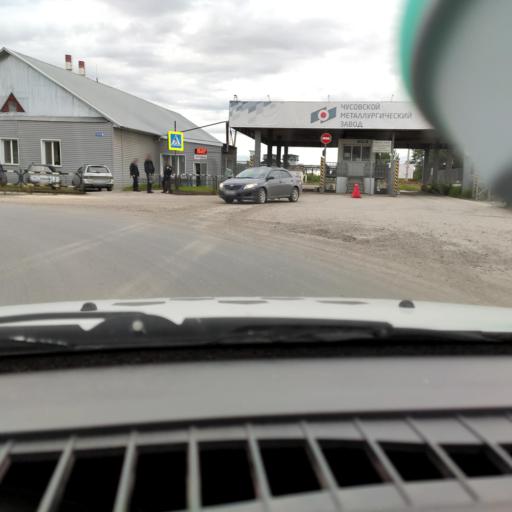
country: RU
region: Perm
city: Chusovoy
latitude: 58.2978
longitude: 57.8108
